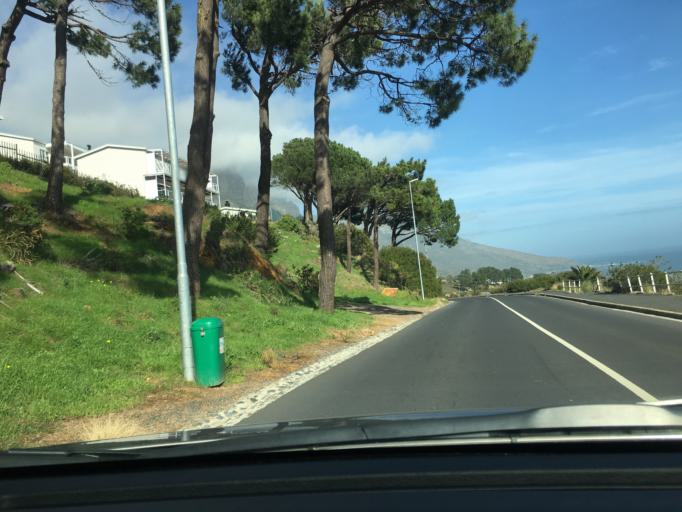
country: ZA
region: Western Cape
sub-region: City of Cape Town
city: Cape Town
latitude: -33.9546
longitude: 18.3861
